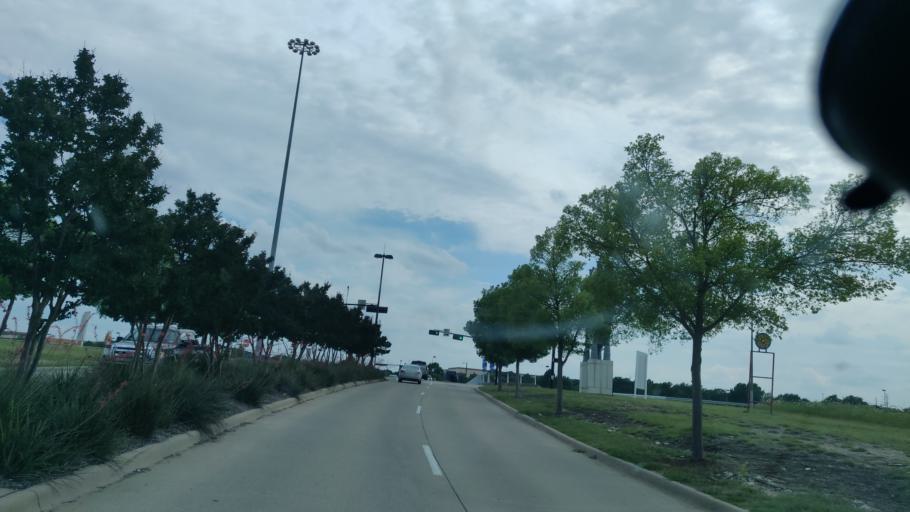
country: US
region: Texas
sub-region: Dallas County
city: Sachse
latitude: 32.9489
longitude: -96.6135
